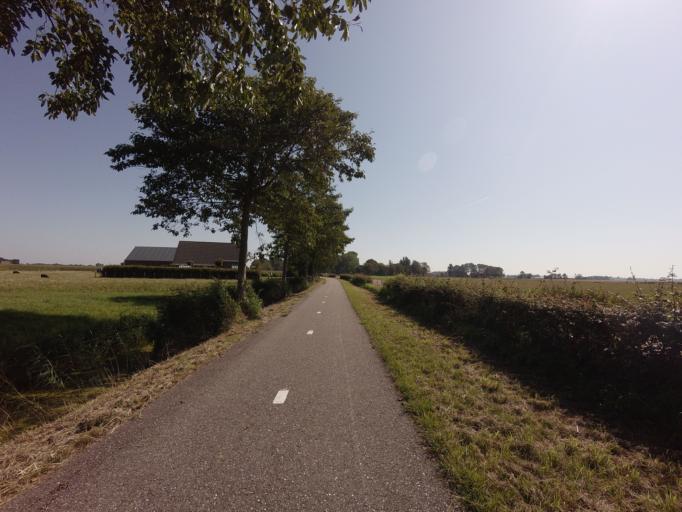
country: NL
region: Friesland
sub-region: Gemeente Dongeradeel
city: Ternaard
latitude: 53.3633
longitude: 5.9749
